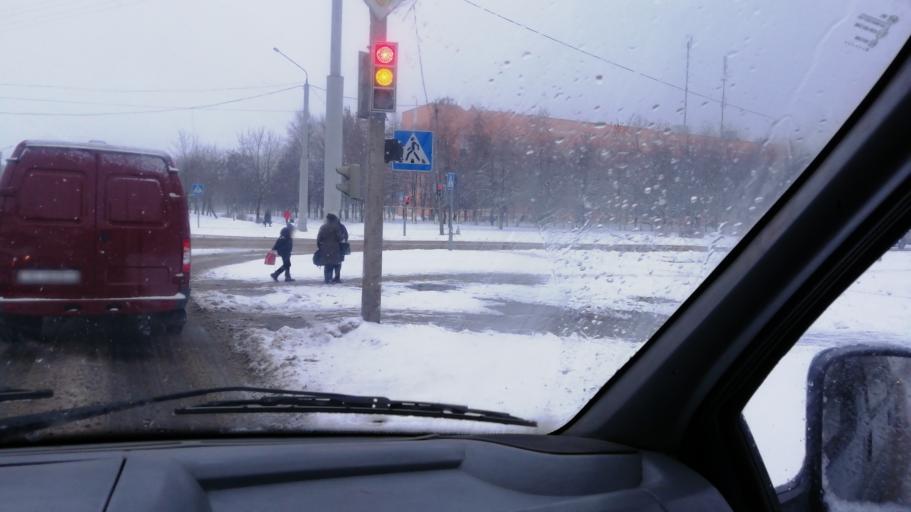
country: BY
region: Mogilev
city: Babruysk
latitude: 53.1750
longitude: 29.1879
